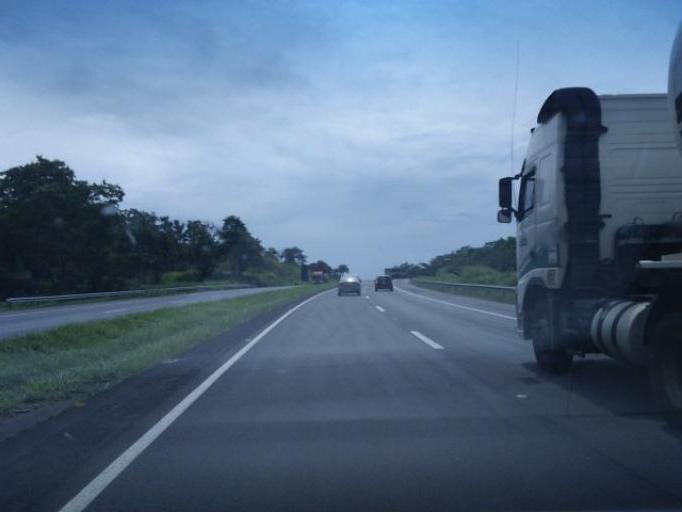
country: BR
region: Sao Paulo
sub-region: Miracatu
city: Miracatu
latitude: -24.3092
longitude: -47.5044
